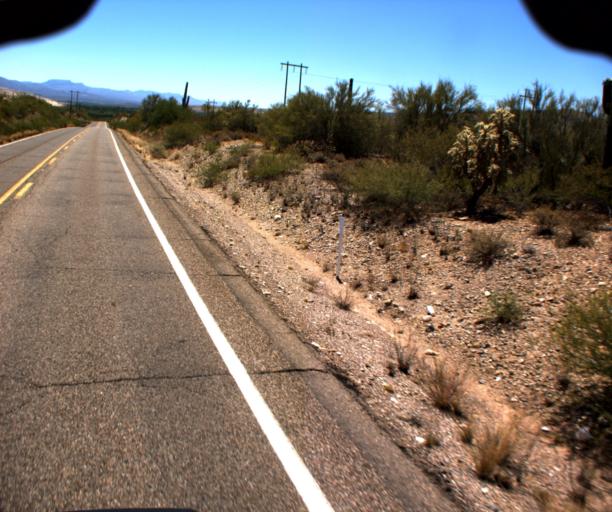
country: US
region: Arizona
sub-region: Pinal County
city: Kearny
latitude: 33.0201
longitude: -110.8498
